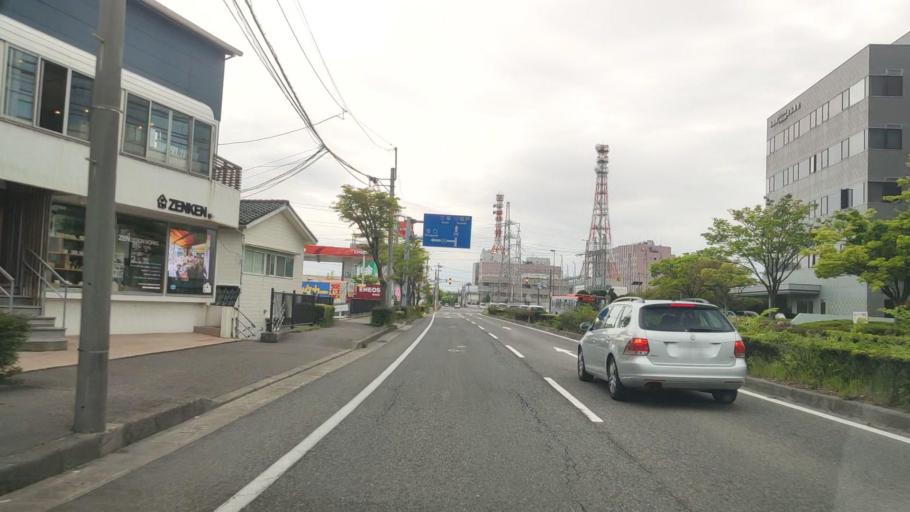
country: JP
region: Niigata
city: Niigata-shi
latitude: 37.8989
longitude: 139.0220
